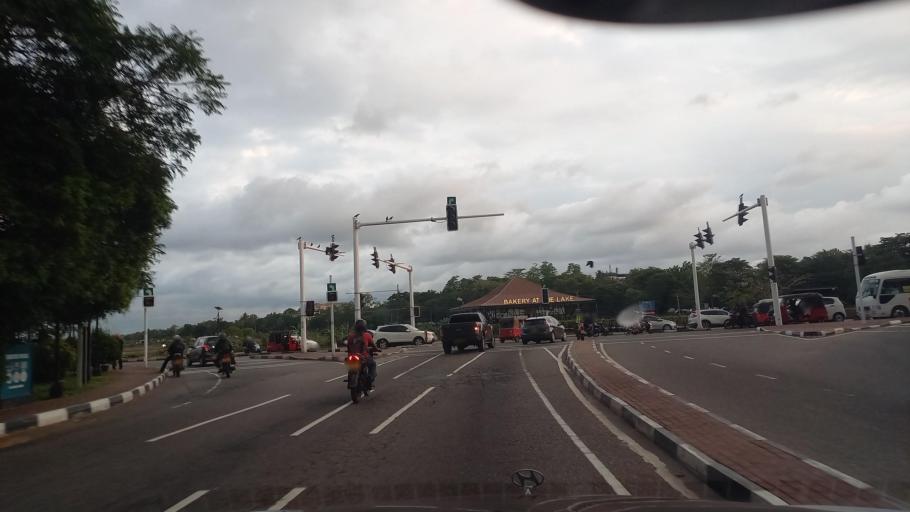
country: LK
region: Western
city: Battaramulla South
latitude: 6.8771
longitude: 79.9283
